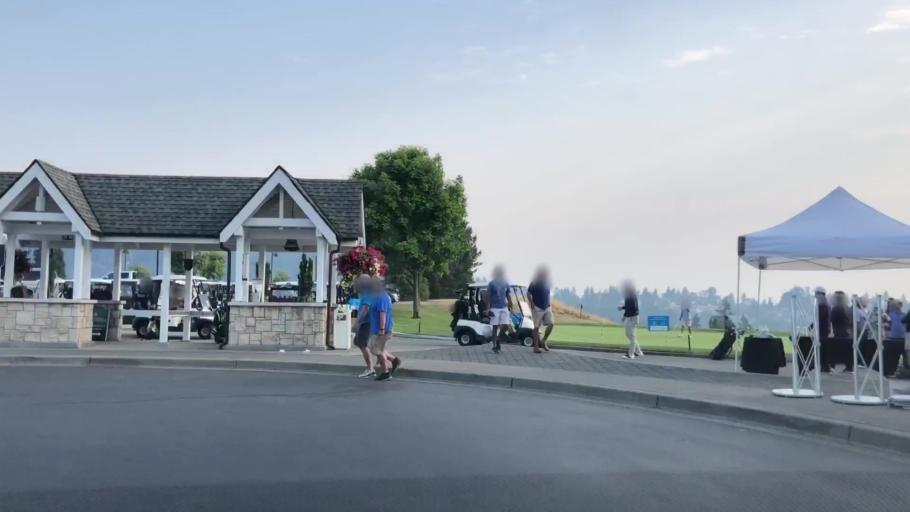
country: US
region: Washington
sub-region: King County
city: Newcastle
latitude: 47.5351
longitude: -122.1436
